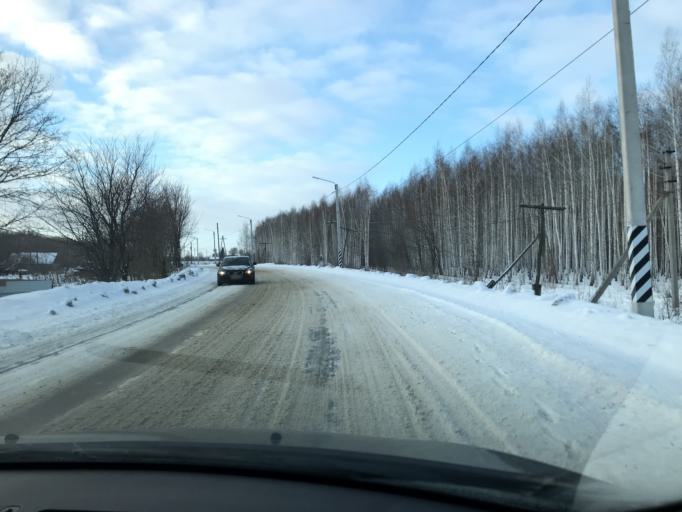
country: RU
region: Ulyanovsk
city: Undory
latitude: 54.6018
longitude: 48.4219
